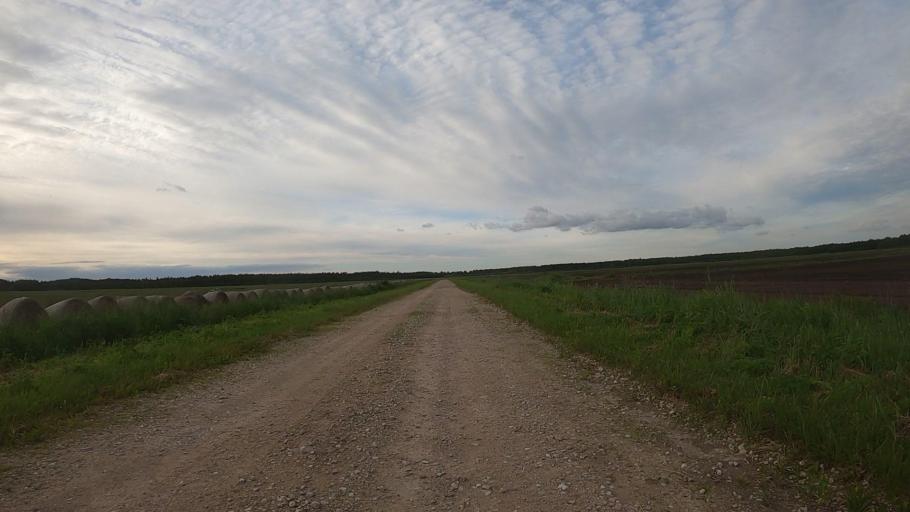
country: LV
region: Olaine
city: Olaine
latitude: 56.8195
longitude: 23.9519
